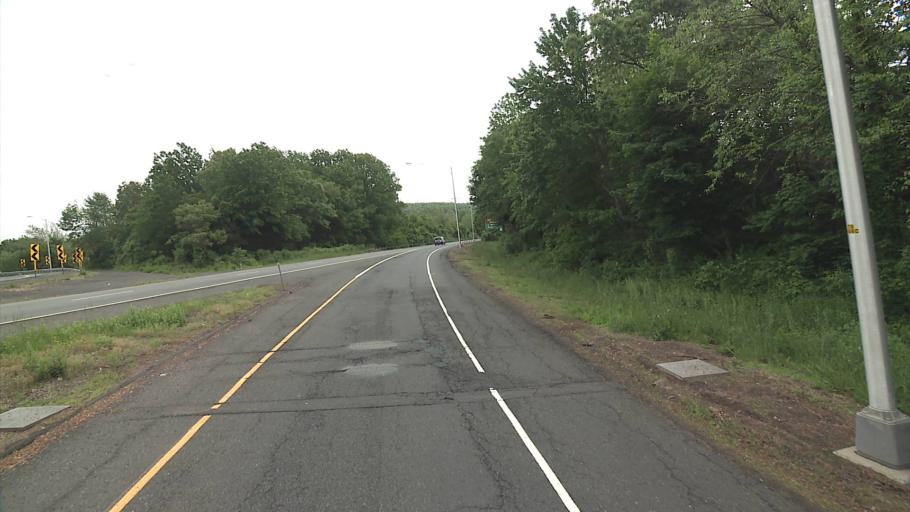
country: US
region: Connecticut
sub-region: New Haven County
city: Meriden
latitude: 41.5366
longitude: -72.7616
